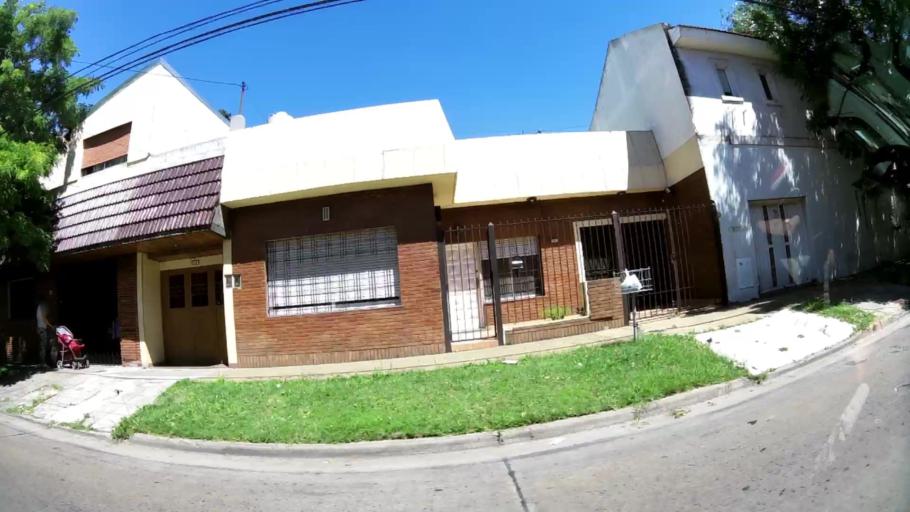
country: AR
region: Buenos Aires
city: Caseros
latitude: -34.5967
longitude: -58.5687
